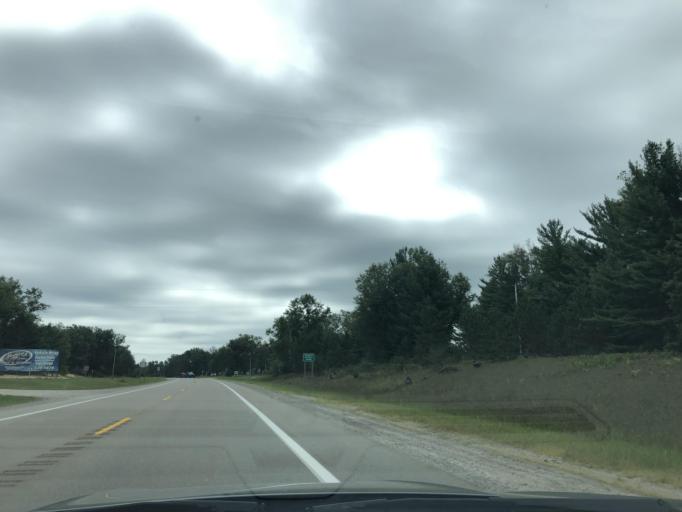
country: US
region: Michigan
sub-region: Clare County
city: Harrison
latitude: 44.0356
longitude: -85.0308
